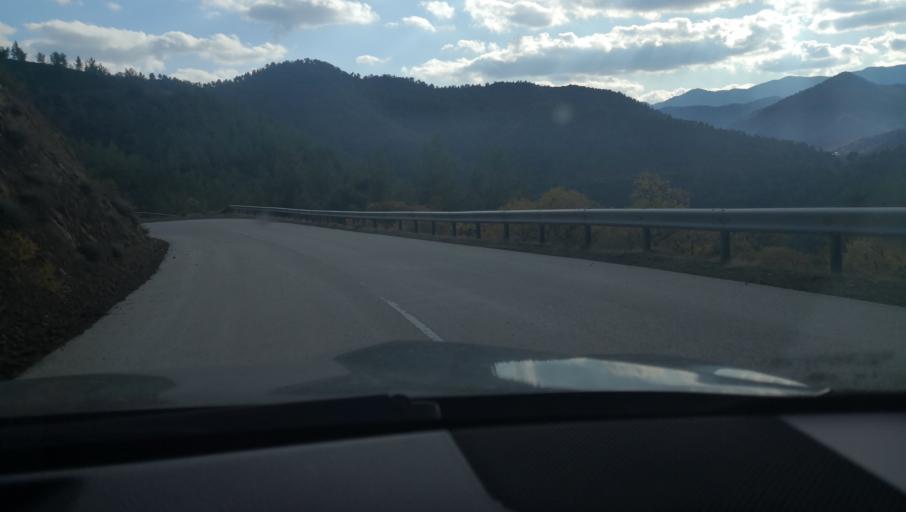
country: CY
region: Lefkosia
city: Lefka
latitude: 35.0606
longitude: 32.7489
